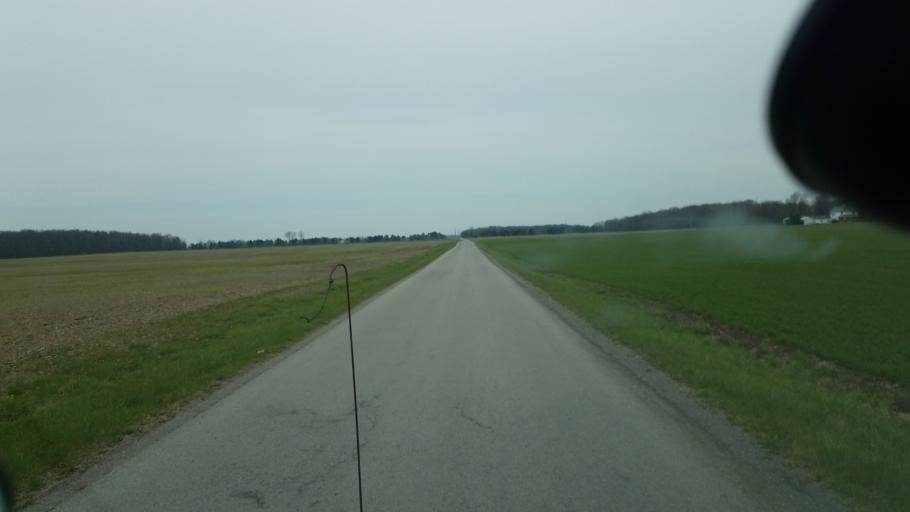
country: US
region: Ohio
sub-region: Wyandot County
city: Carey
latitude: 40.9720
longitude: -83.5129
